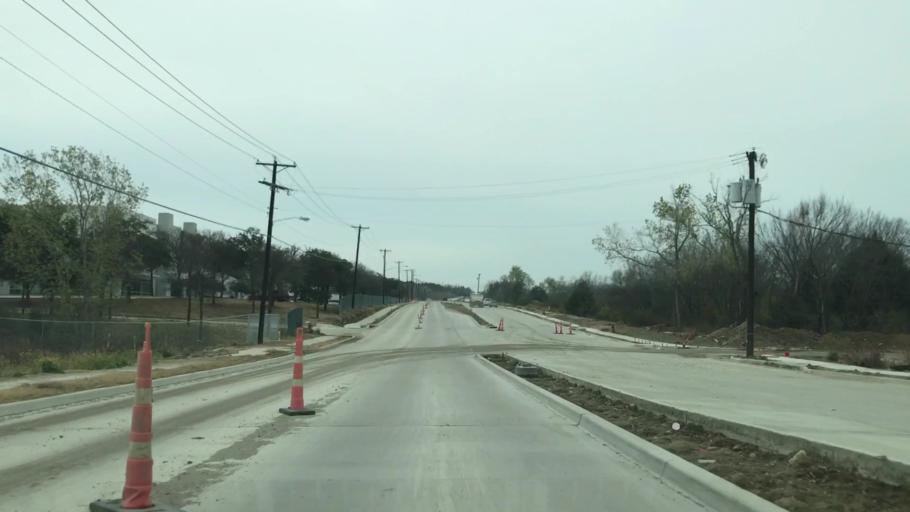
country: US
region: Texas
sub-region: Dallas County
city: Cockrell Hill
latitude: 32.7620
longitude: -96.9022
